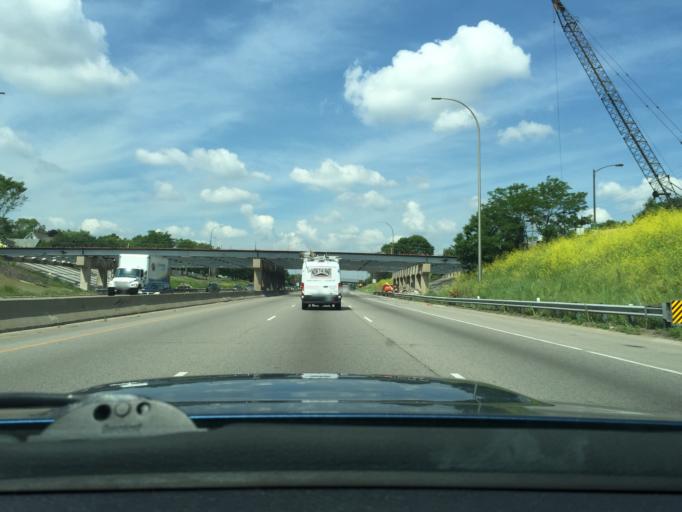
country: US
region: Minnesota
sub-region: Ramsey County
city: Falcon Heights
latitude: 44.9517
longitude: -93.1656
